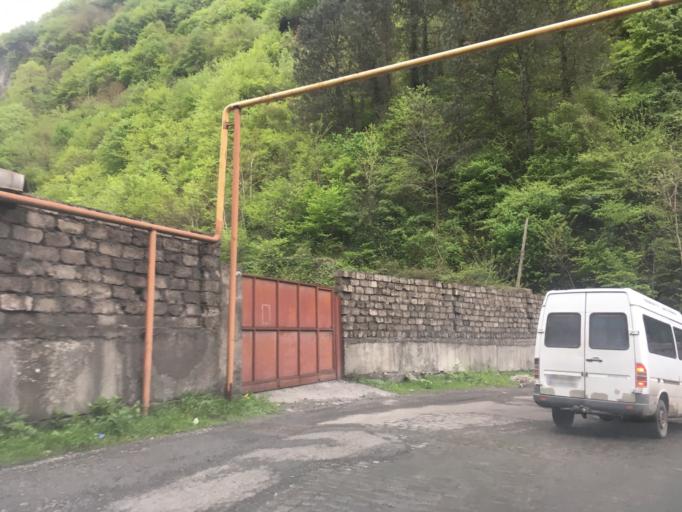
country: GE
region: Racha-Lechkhumi and Kvemo Svaneti
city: Gori
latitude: 42.2904
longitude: 43.2997
